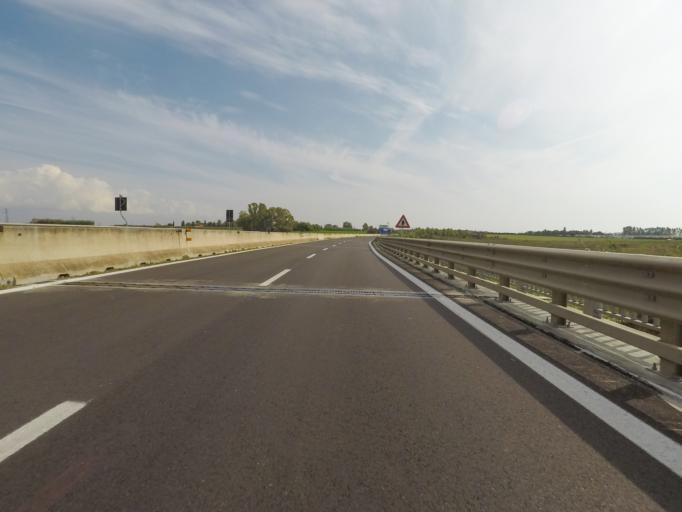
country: IT
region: Latium
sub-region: Provincia di Viterbo
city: Pescia Romana
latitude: 42.4125
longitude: 11.4756
